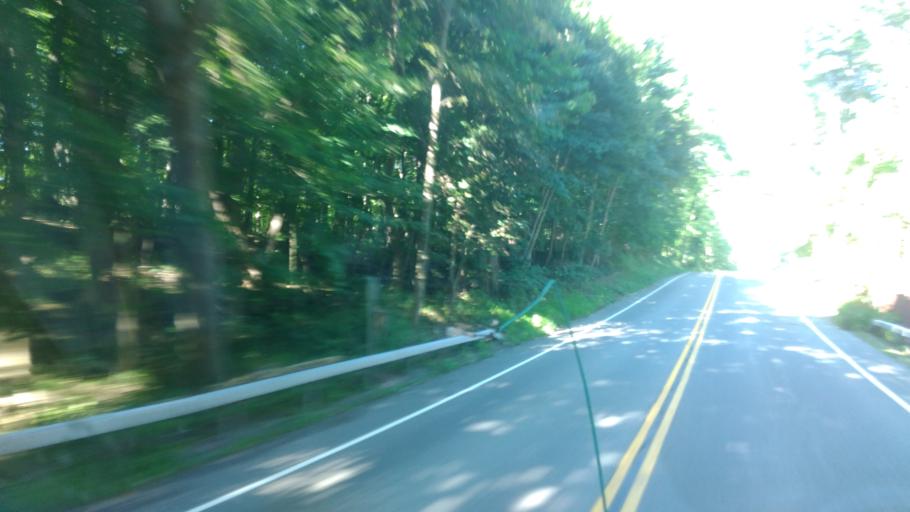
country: US
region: New York
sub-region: Monroe County
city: Webster
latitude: 43.2573
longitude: -77.4631
